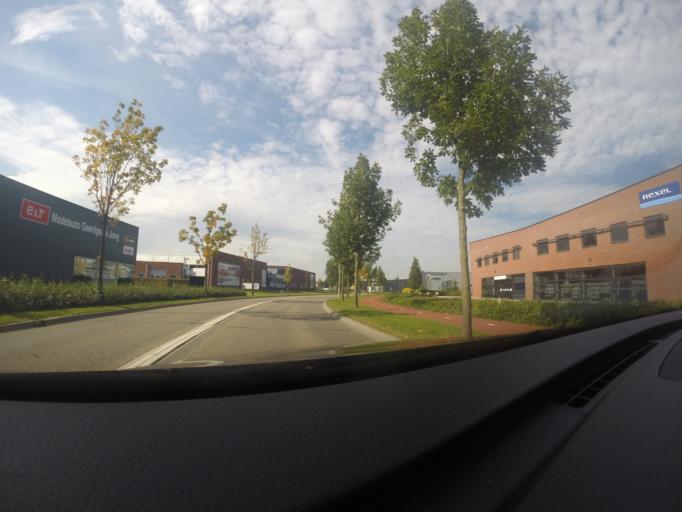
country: NL
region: Gelderland
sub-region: Gemeente Doetinchem
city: Doetinchem
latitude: 51.9476
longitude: 6.2808
